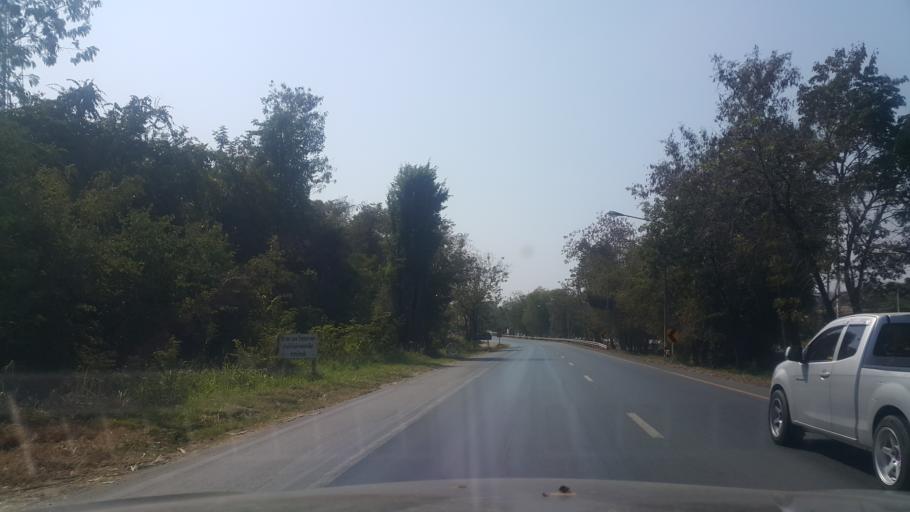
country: TH
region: Nakhon Ratchasima
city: Pak Thong Chai
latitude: 14.6214
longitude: 102.0069
